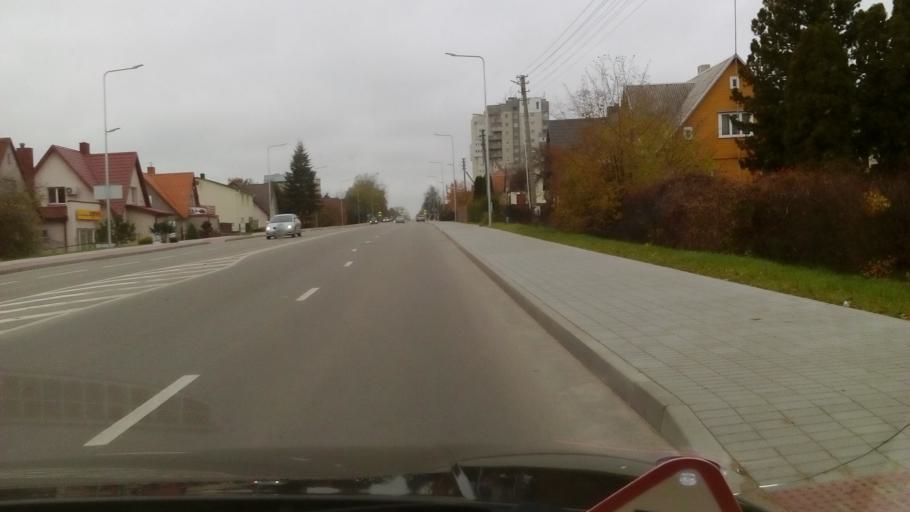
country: LT
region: Marijampoles apskritis
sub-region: Marijampole Municipality
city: Marijampole
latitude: 54.5611
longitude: 23.3391
